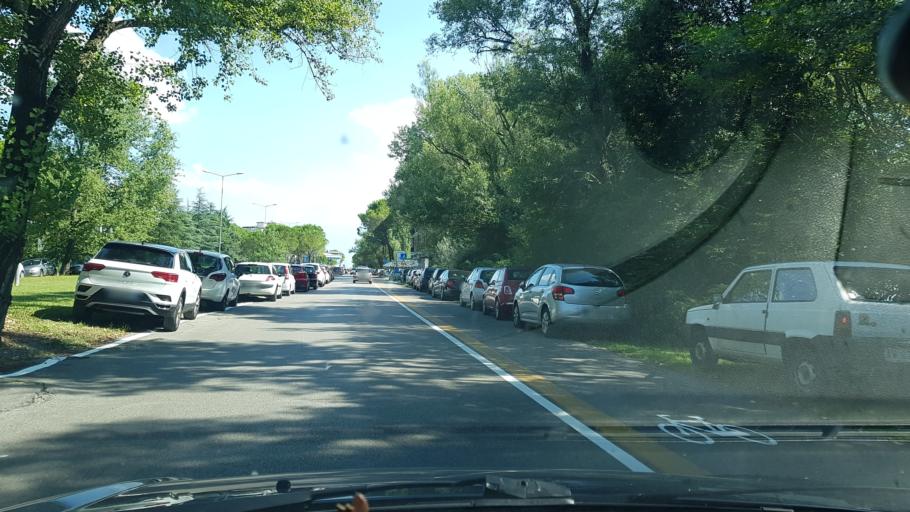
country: IT
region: Friuli Venezia Giulia
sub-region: Provincia di Gorizia
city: Monfalcone
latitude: 45.7780
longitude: 13.5254
